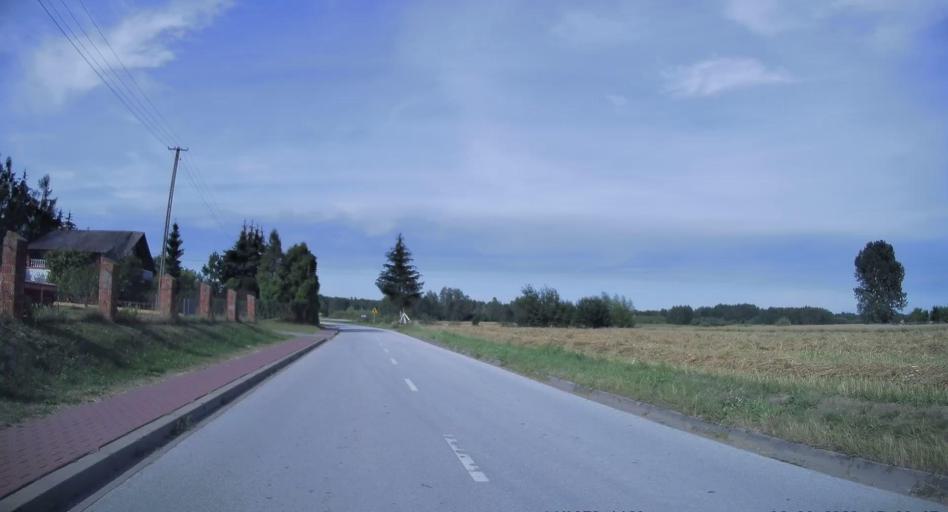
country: PL
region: Lodz Voivodeship
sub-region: Powiat opoczynski
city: Mniszkow
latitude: 51.3335
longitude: 20.0311
